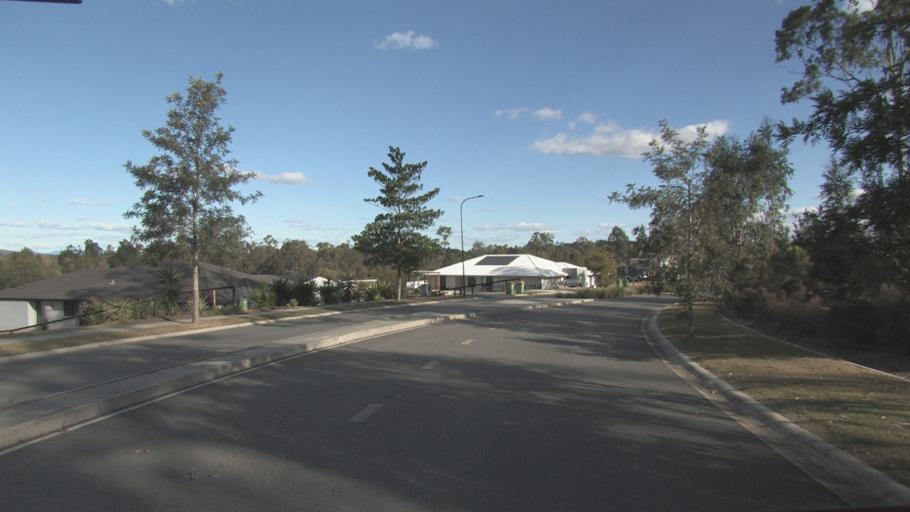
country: AU
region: Queensland
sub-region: Logan
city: North Maclean
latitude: -27.8244
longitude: 152.9800
